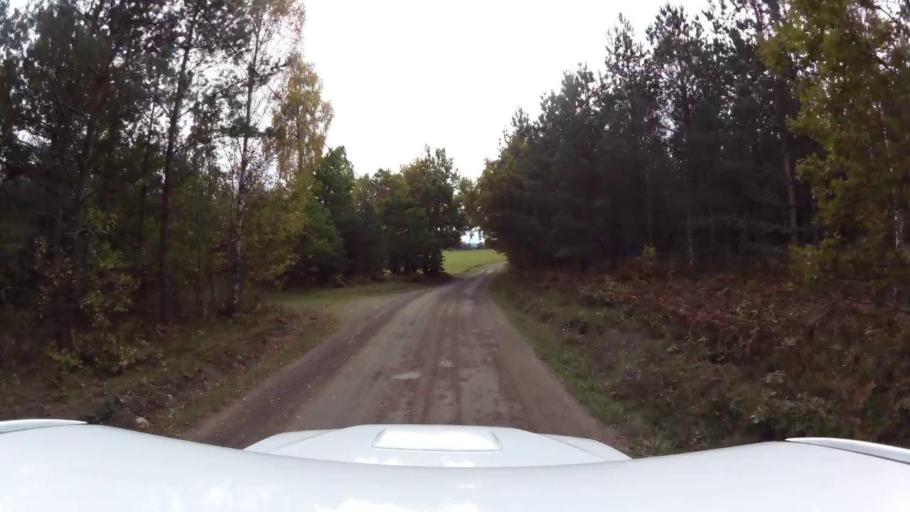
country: SE
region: OEstergoetland
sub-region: Linkopings Kommun
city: Ekangen
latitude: 58.5500
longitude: 15.6630
